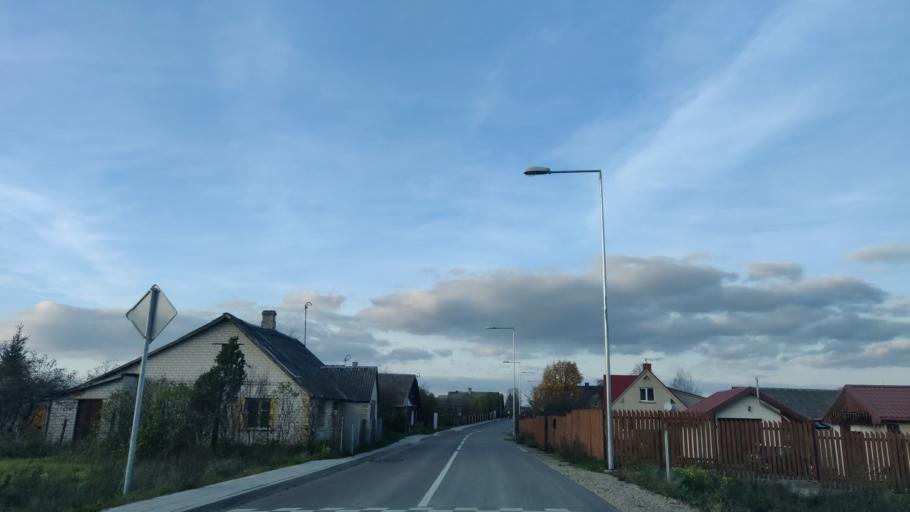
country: LT
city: Lentvaris
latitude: 54.5817
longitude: 25.0514
